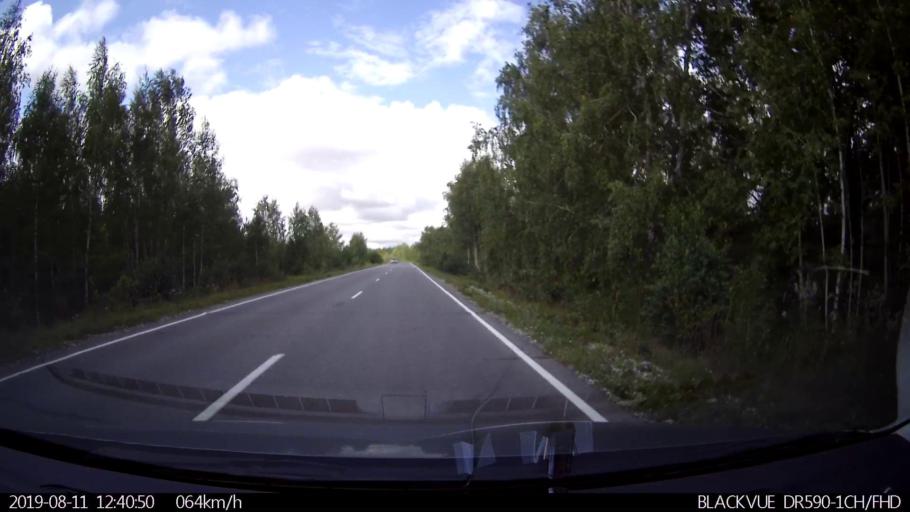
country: RU
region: Ulyanovsk
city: Ignatovka
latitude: 53.8408
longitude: 47.7752
